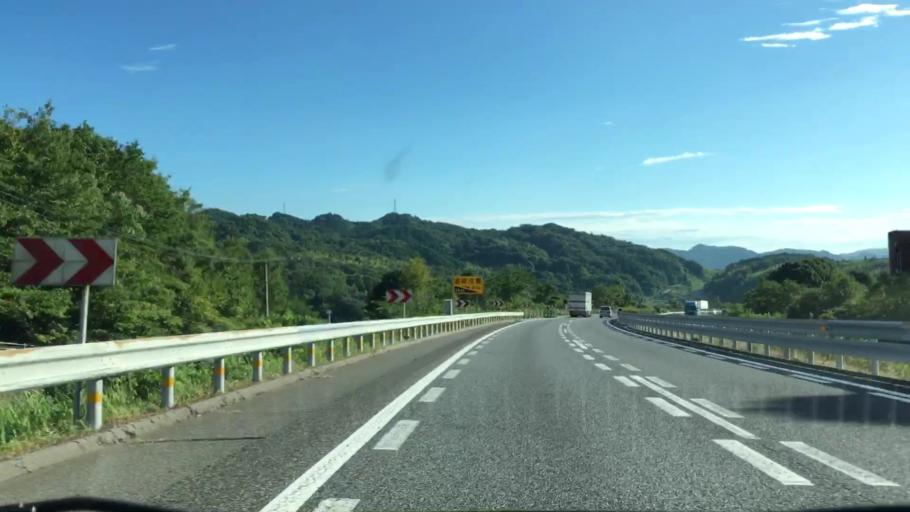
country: JP
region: Yamaguchi
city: Iwakuni
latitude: 34.1064
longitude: 132.1130
